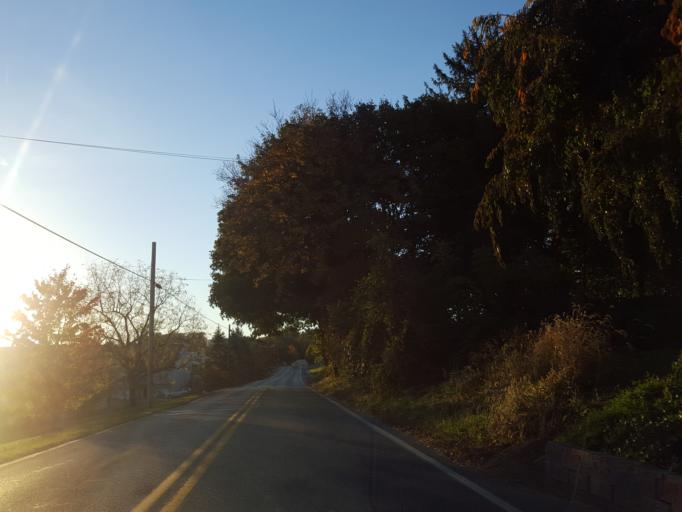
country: US
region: Pennsylvania
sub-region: York County
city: Red Lion
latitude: 39.8958
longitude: -76.6192
